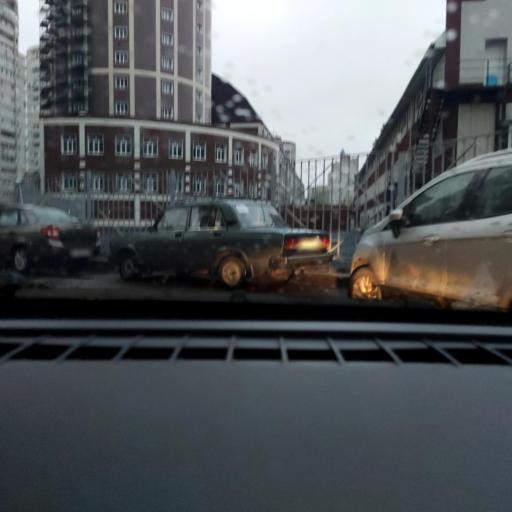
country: RU
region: Voronezj
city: Voronezh
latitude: 51.7123
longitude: 39.1859
